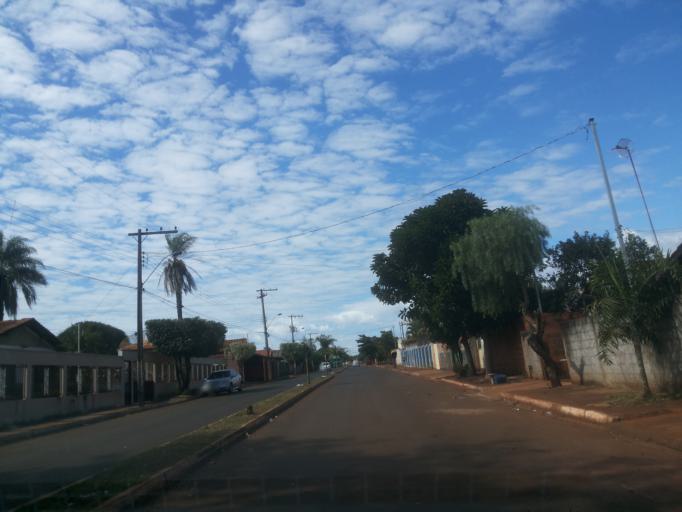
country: BR
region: Minas Gerais
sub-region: Centralina
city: Centralina
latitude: -18.5807
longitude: -49.2080
